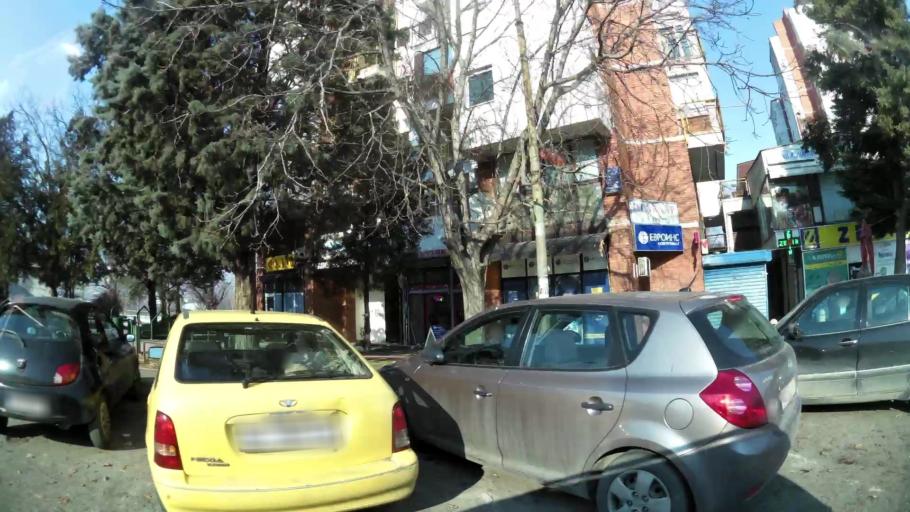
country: MK
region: Karpos
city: Skopje
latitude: 41.9895
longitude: 21.4586
